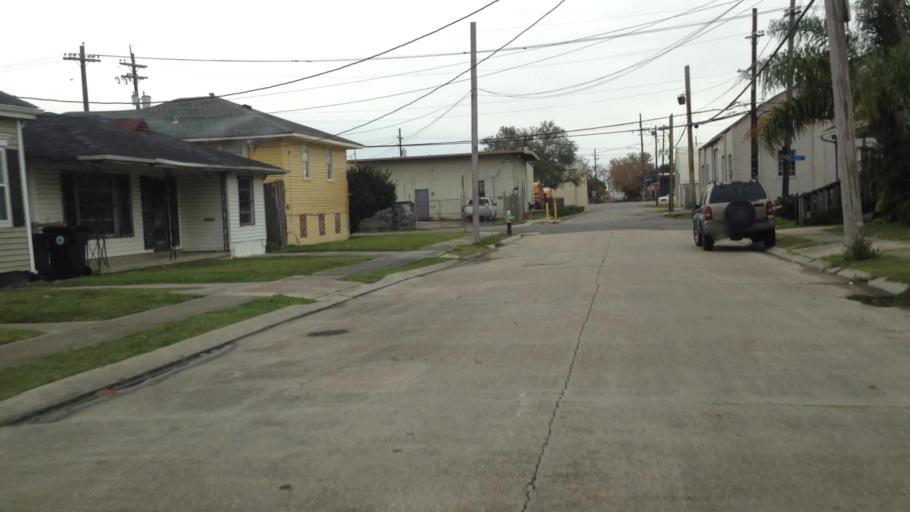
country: US
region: Louisiana
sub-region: Orleans Parish
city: New Orleans
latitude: 29.9537
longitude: -90.1043
